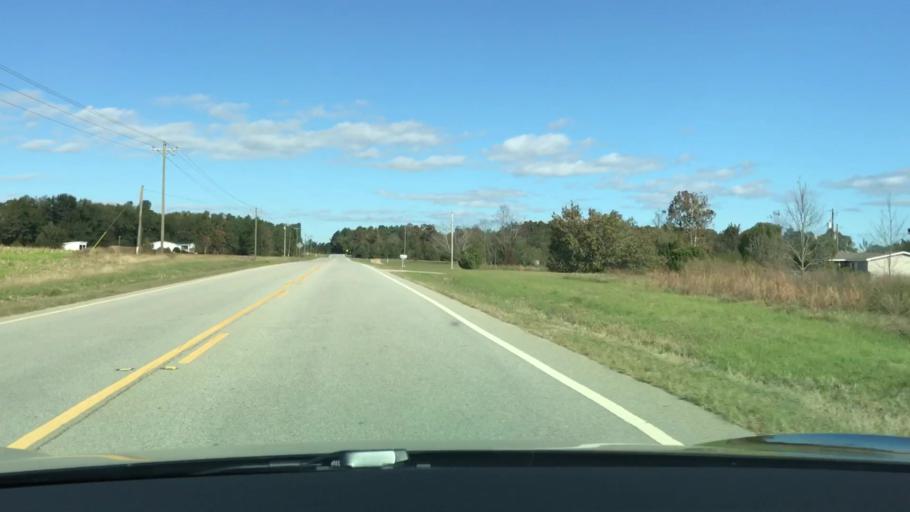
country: US
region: Georgia
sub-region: Jefferson County
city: Wrens
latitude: 33.1812
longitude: -82.4536
